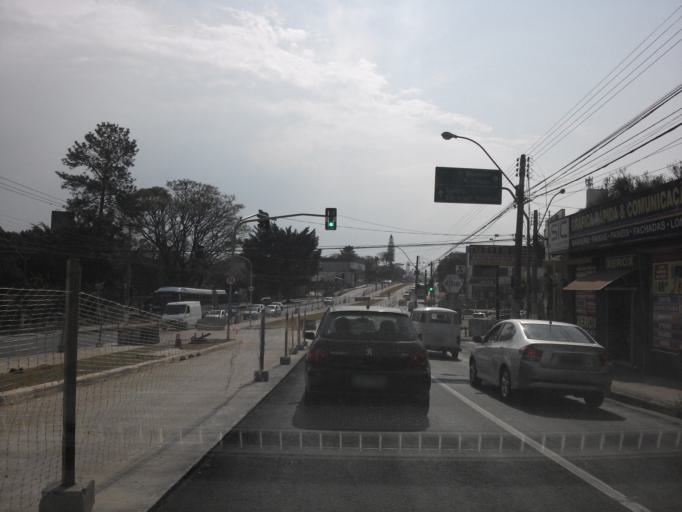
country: BR
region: Sao Paulo
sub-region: Campinas
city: Campinas
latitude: -22.9224
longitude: -47.0784
